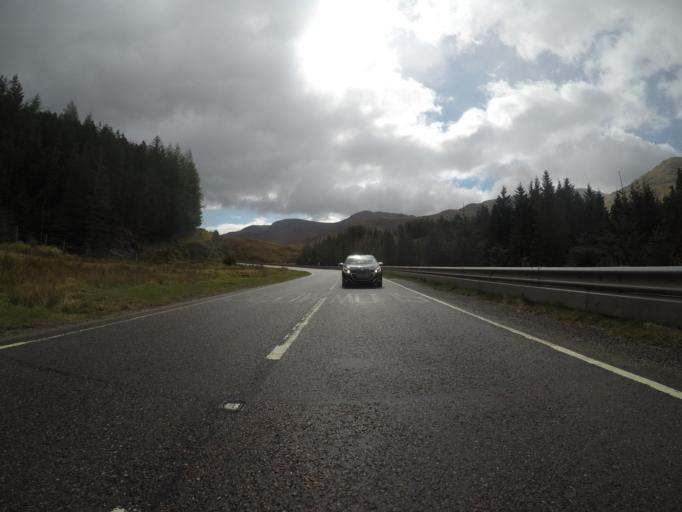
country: GB
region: Scotland
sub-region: Highland
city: Fort William
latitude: 57.1571
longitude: -5.2565
